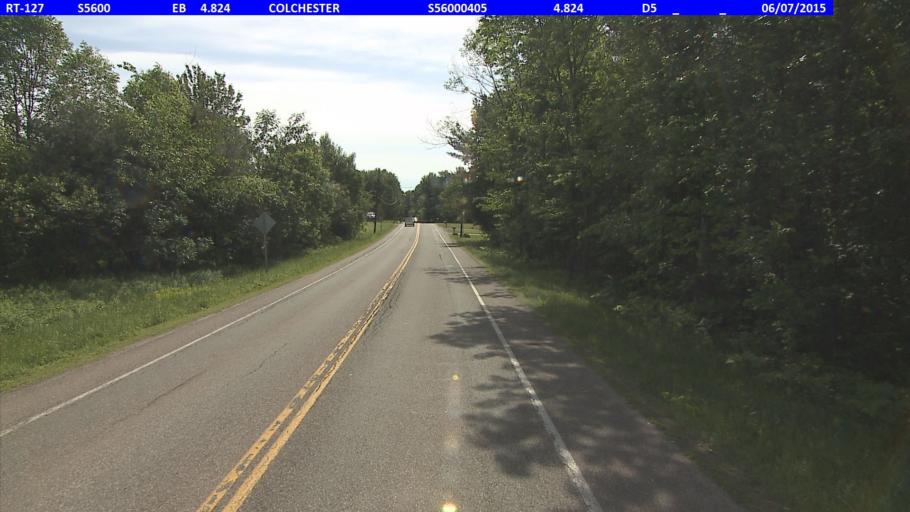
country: US
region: Vermont
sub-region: Chittenden County
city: Winooski
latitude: 44.5298
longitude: -73.1920
